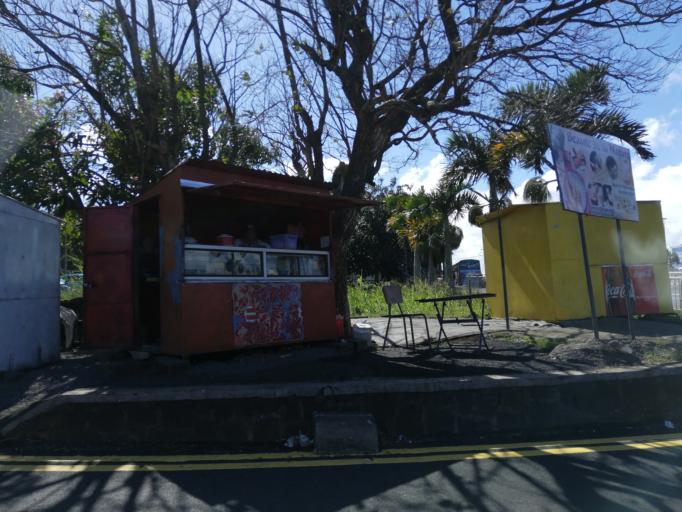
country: MU
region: Moka
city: Moka
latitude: -20.2322
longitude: 57.4981
